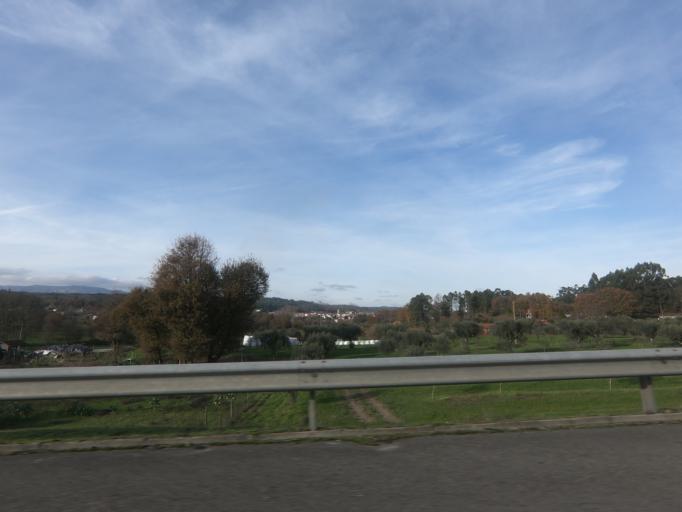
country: PT
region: Viseu
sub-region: Concelho de Tondela
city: Tondela
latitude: 40.5792
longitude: -8.0241
